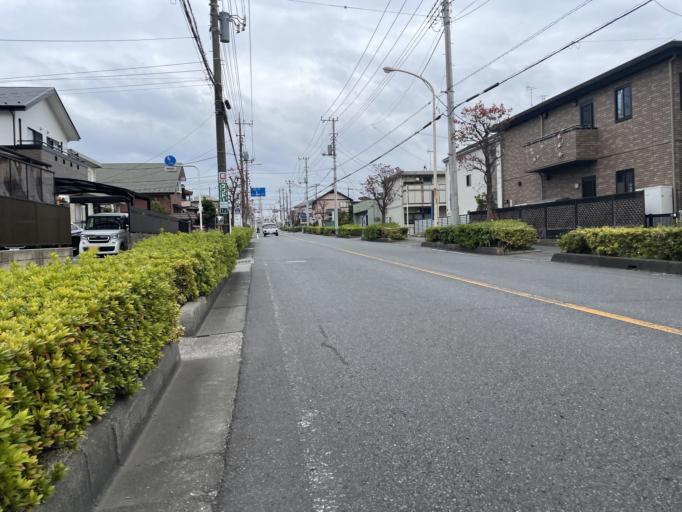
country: JP
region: Saitama
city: Shiraoka
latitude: 35.9965
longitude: 139.6588
